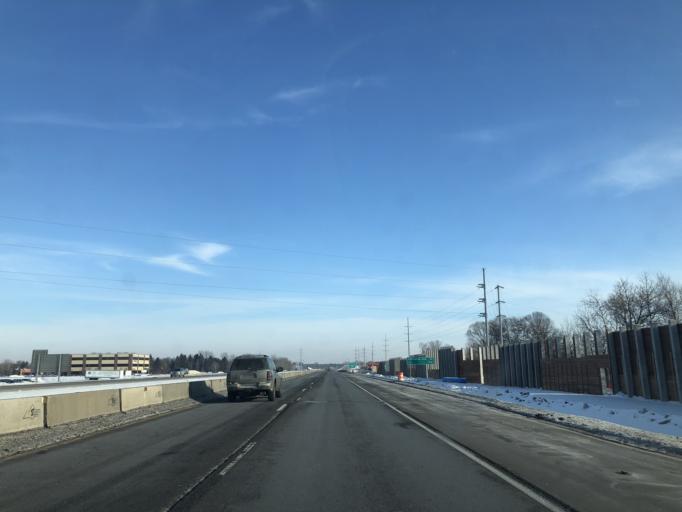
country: US
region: Minnesota
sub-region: Anoka County
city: Lexington
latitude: 45.1526
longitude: -93.1725
